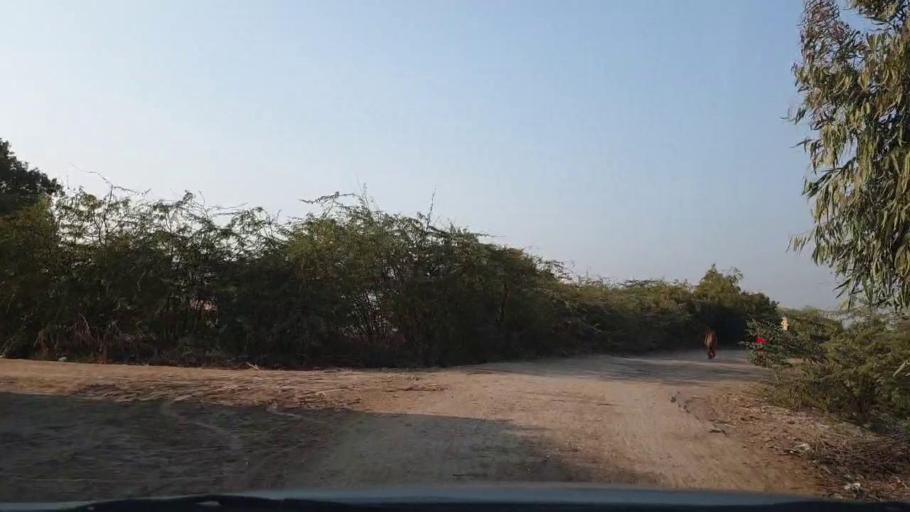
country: PK
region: Sindh
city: Tando Adam
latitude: 25.6817
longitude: 68.6333
